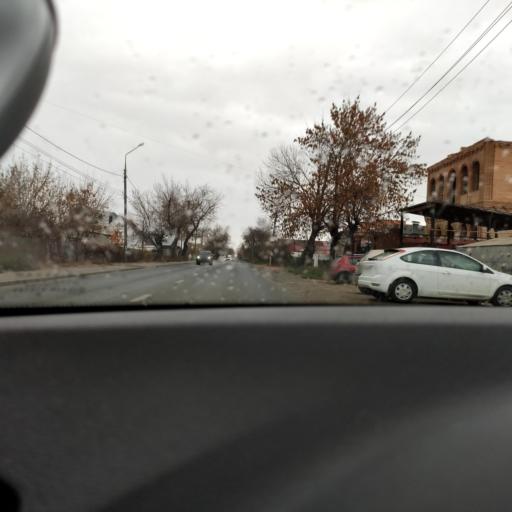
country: RU
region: Samara
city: Smyshlyayevka
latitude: 53.2359
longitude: 50.3167
